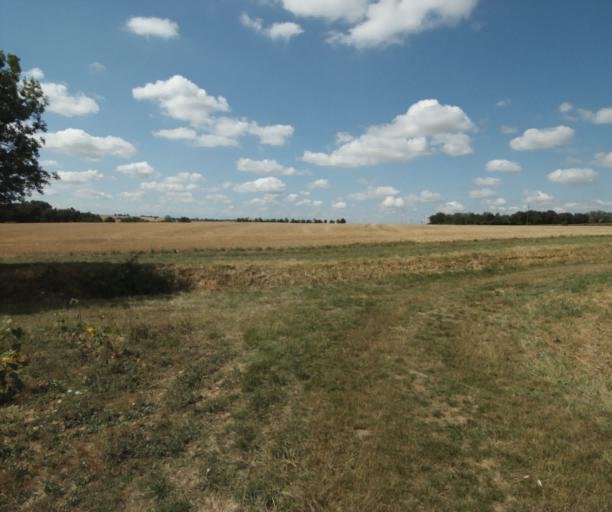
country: FR
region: Midi-Pyrenees
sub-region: Departement de la Haute-Garonne
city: Auriac-sur-Vendinelle
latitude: 43.4527
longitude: 1.8041
